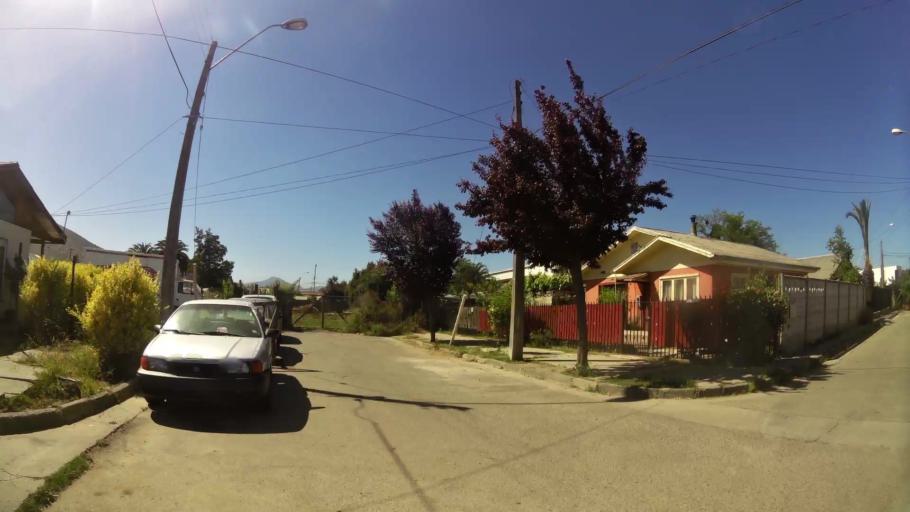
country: CL
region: Valparaiso
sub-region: Provincia de Marga Marga
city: Quilpue
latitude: -33.3163
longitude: -71.4046
